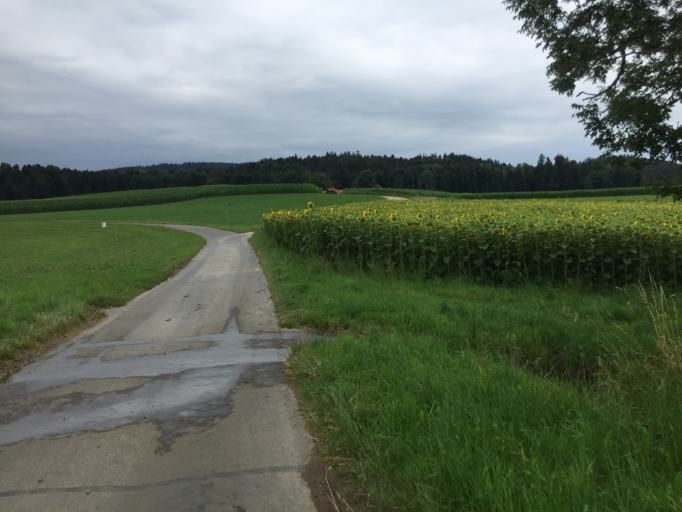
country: CH
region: Bern
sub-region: Bern-Mittelland District
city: Worb
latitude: 46.9164
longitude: 7.5929
